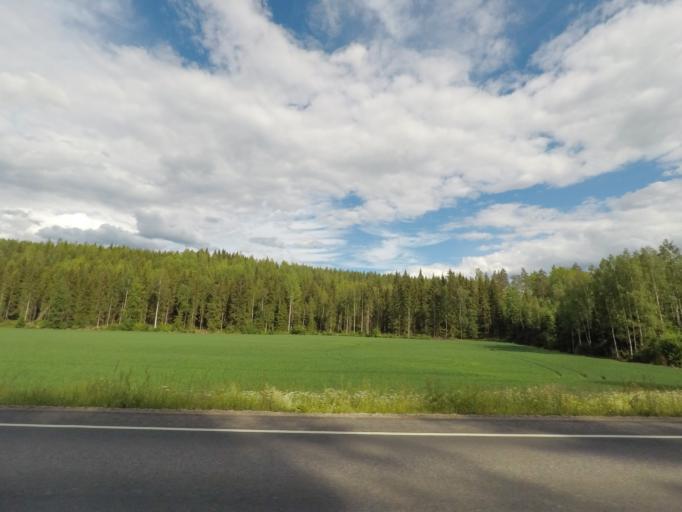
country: FI
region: Uusimaa
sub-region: Porvoo
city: Pukkila
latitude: 60.7859
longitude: 25.4614
